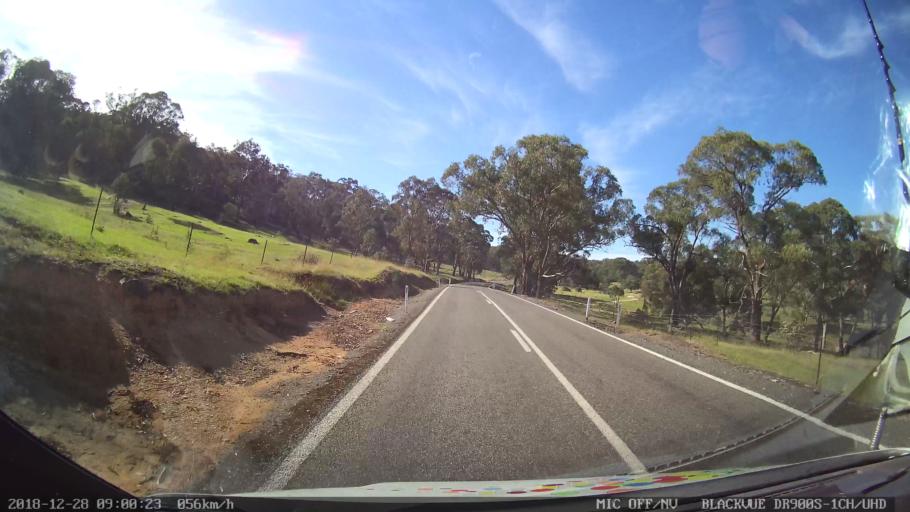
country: AU
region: New South Wales
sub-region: Upper Lachlan Shire
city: Crookwell
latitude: -34.1379
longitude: 149.3345
